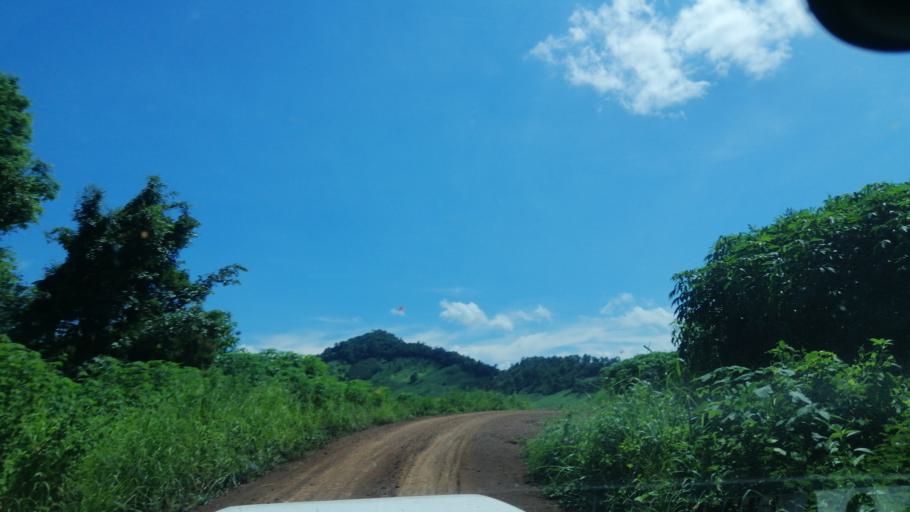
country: TH
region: Uttaradit
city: Ban Khok
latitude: 18.0970
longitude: 101.2512
